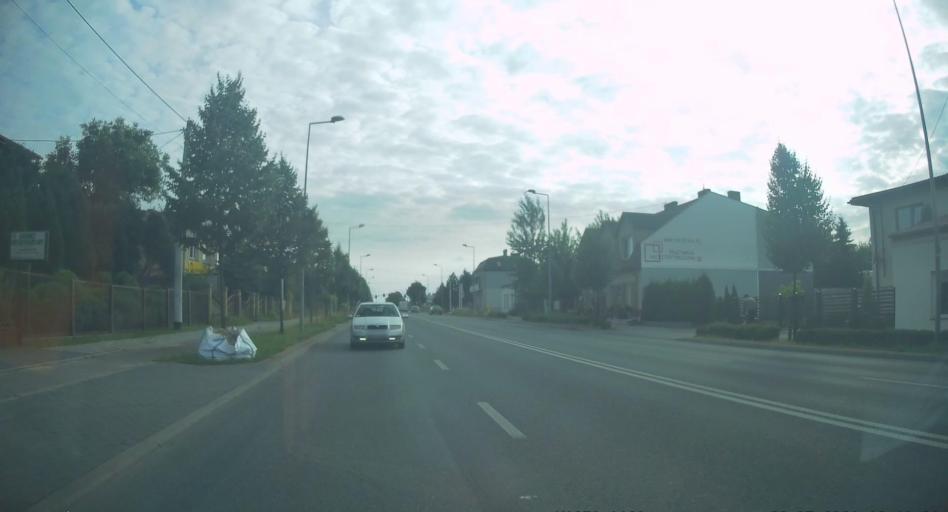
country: PL
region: Silesian Voivodeship
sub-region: Czestochowa
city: Czestochowa
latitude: 50.8386
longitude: 19.1580
